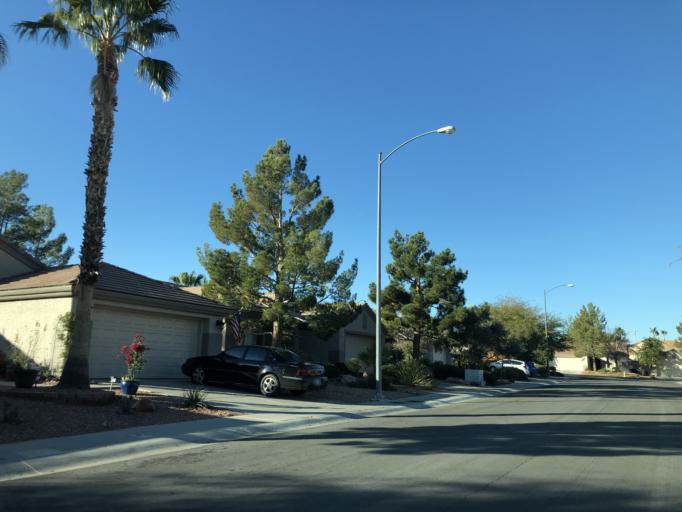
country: US
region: Nevada
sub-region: Clark County
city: Whitney
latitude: 36.0119
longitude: -115.0814
